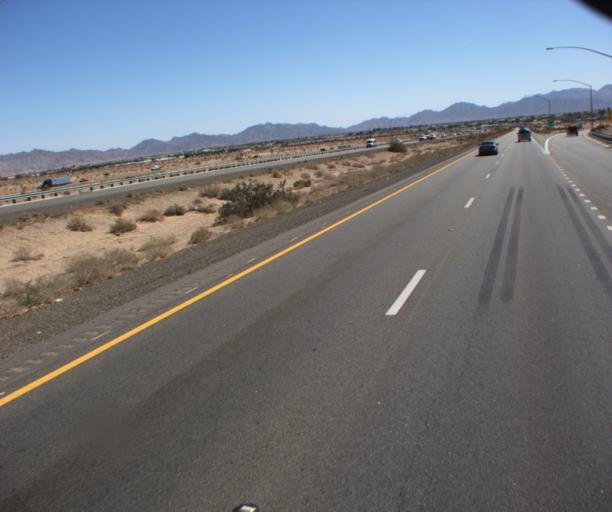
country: US
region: Arizona
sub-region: Yuma County
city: Fortuna Foothills
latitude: 32.6733
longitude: -114.4903
